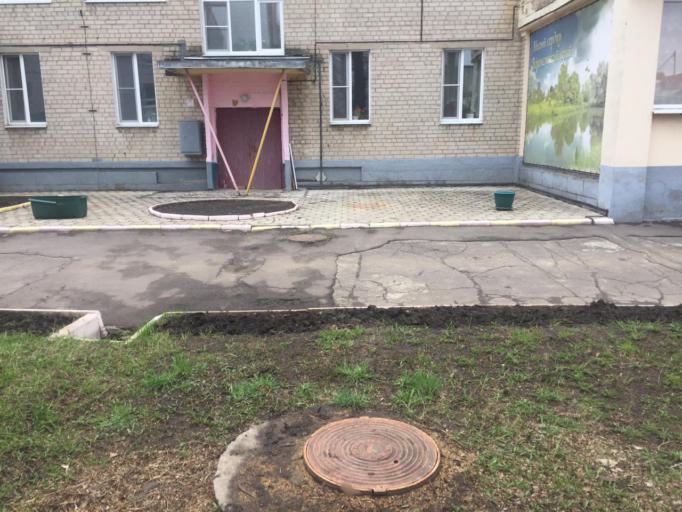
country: RU
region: Voronezj
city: Voronezh
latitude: 51.6797
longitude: 39.1529
